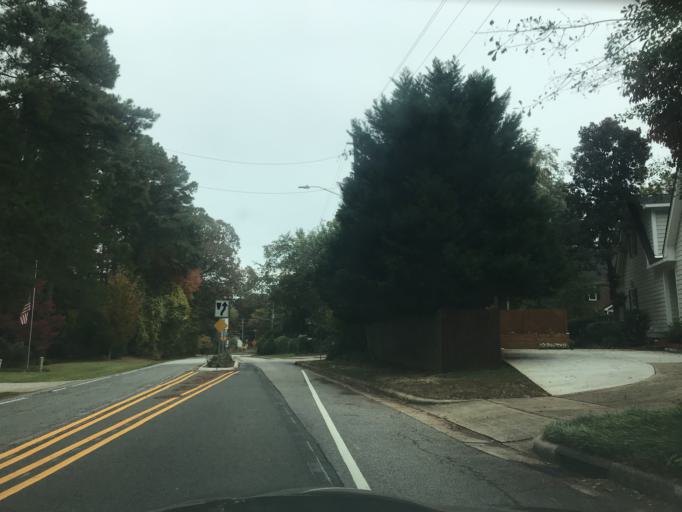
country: US
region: North Carolina
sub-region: Wake County
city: West Raleigh
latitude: 35.8520
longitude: -78.6752
